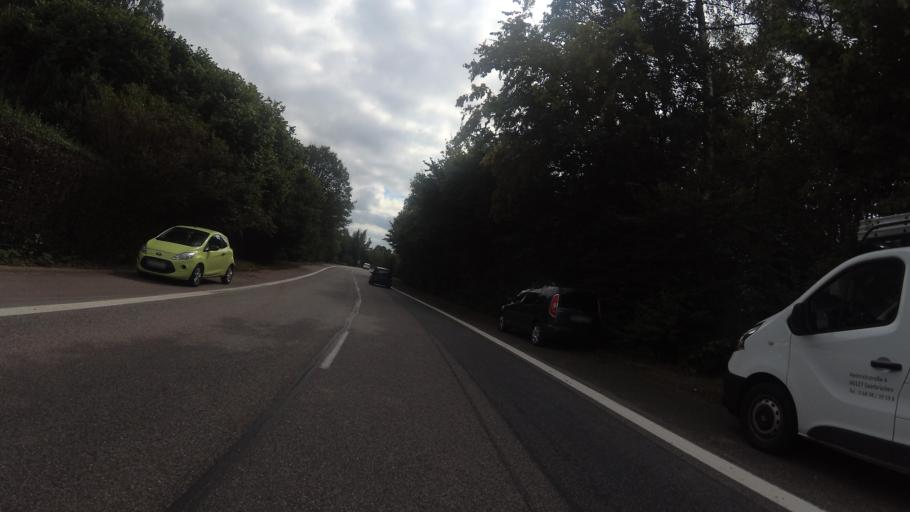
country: DE
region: Saarland
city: Grossrosseln
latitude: 49.1978
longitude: 6.8127
